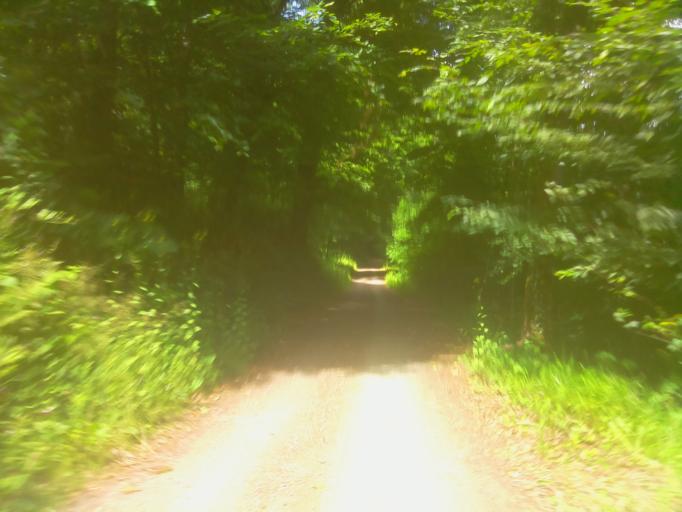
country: DE
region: Hesse
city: Hirschhorn
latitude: 49.4421
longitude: 8.9040
